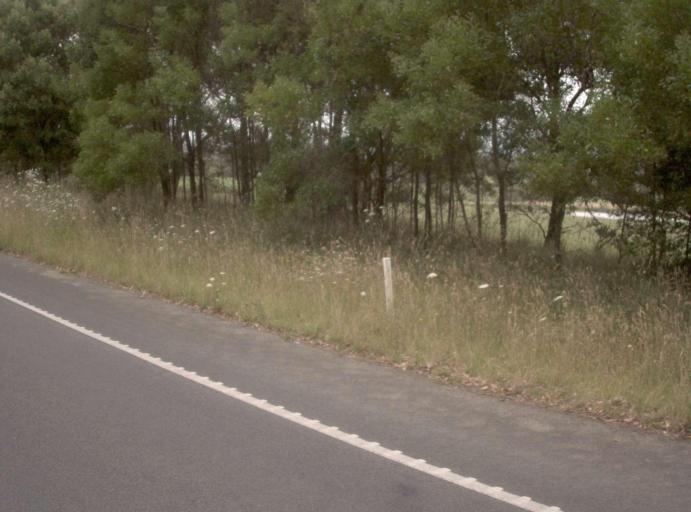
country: AU
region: Victoria
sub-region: Cardinia
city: Bunyip
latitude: -38.2038
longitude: 145.7542
